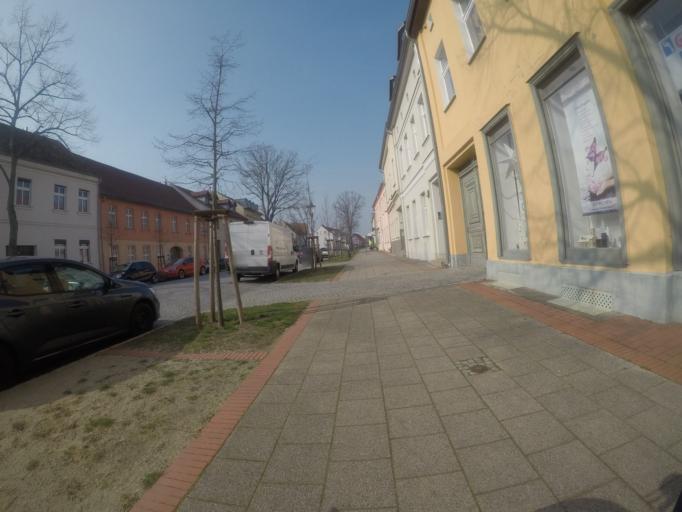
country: DE
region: Brandenburg
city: Mittenwalde
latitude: 52.2630
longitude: 13.5372
